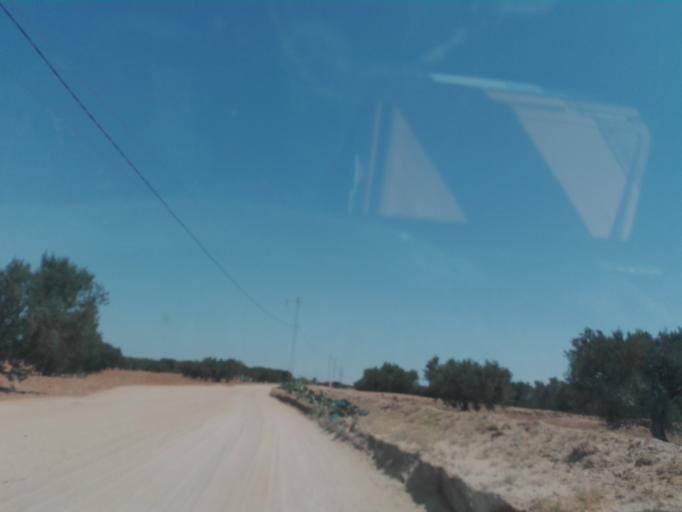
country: TN
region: Safaqis
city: Bi'r `Ali Bin Khalifah
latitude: 34.6695
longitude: 10.2359
